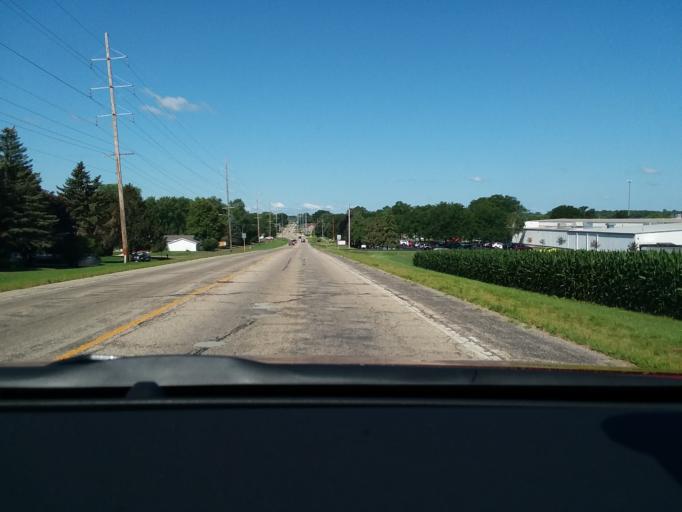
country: US
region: Wisconsin
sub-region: Dane County
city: De Forest
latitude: 43.2529
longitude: -89.3324
